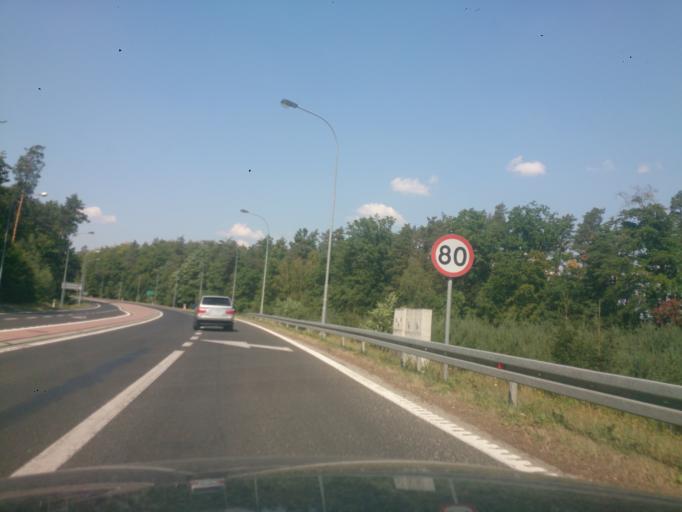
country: PL
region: Subcarpathian Voivodeship
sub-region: Powiat rzeszowski
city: Glogow Malopolski
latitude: 50.1714
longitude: 21.9403
